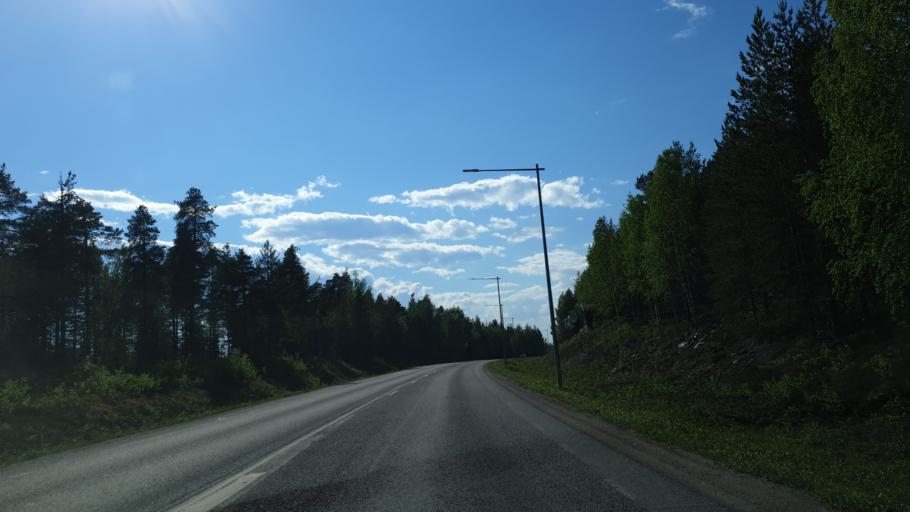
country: SE
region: Norrbotten
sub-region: Pitea Kommun
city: Pitea
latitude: 65.3309
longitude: 21.4547
